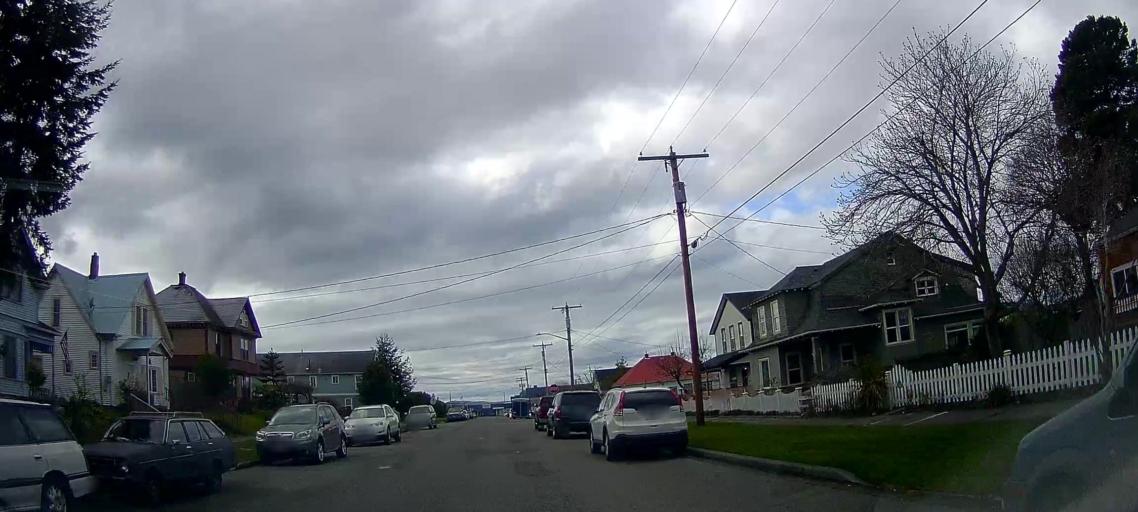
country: US
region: Washington
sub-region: Skagit County
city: Anacortes
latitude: 48.5191
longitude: -122.6147
